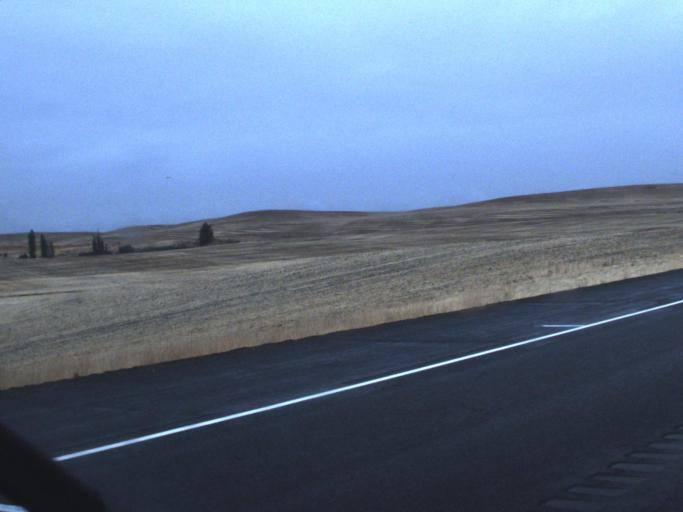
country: US
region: Washington
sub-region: Spokane County
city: Cheney
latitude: 47.4150
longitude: -117.3917
